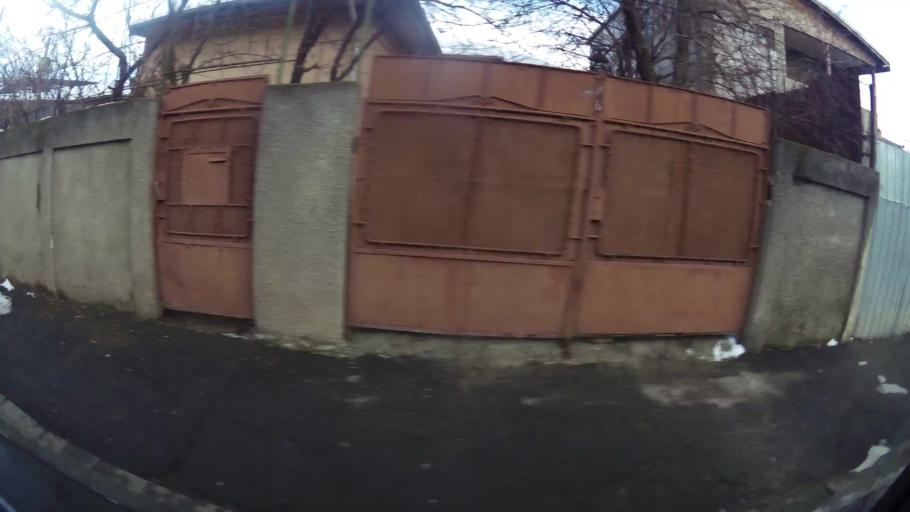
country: RO
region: Bucuresti
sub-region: Municipiul Bucuresti
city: Bucuresti
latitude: 44.3920
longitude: 26.0747
